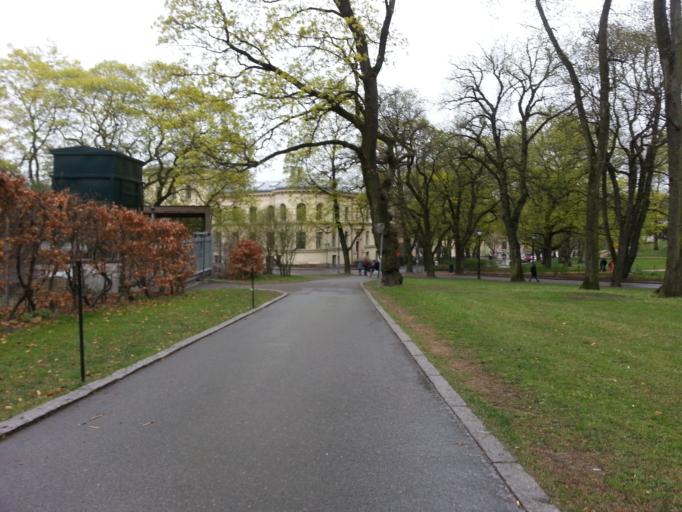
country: NO
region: Oslo
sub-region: Oslo
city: Oslo
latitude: 59.9173
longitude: 10.7310
